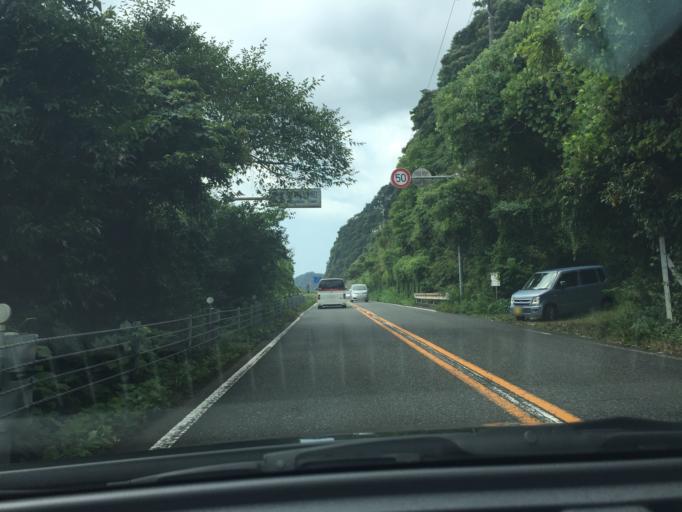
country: JP
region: Shizuoka
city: Ito
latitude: 34.8527
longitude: 139.0823
